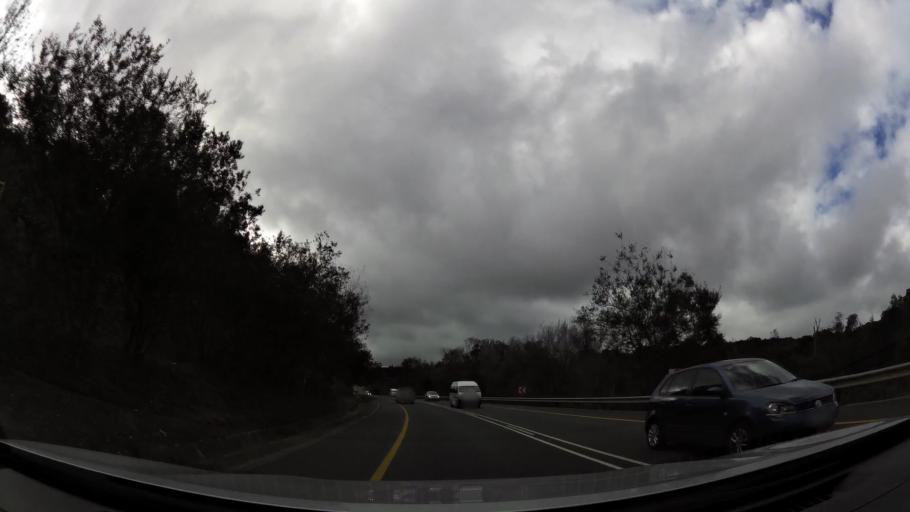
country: ZA
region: Western Cape
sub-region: Eden District Municipality
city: Knysna
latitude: -34.0338
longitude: 23.1585
